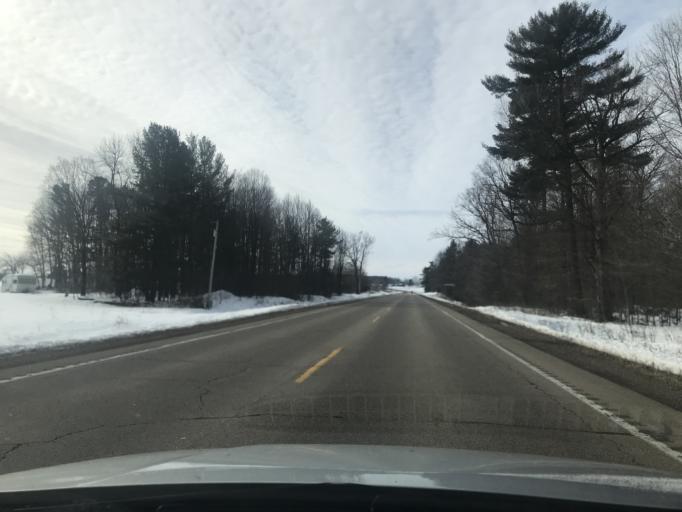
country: US
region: Wisconsin
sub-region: Oconto County
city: Gillett
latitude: 44.8841
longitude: -88.3369
